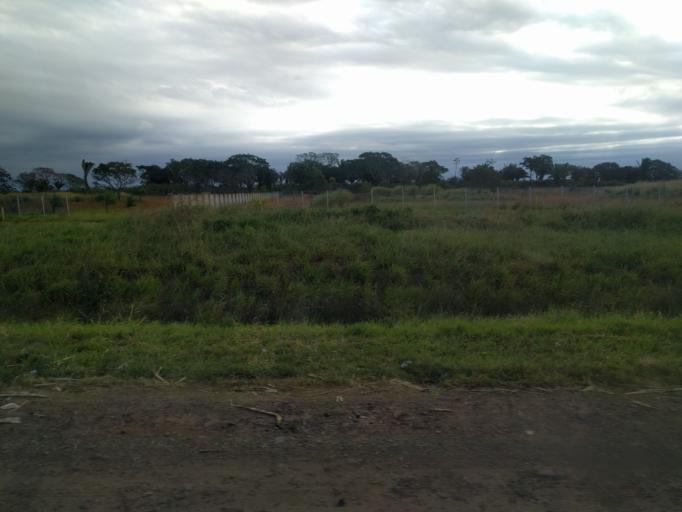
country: BO
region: Santa Cruz
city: La Belgica
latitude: -17.5933
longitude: -63.1585
